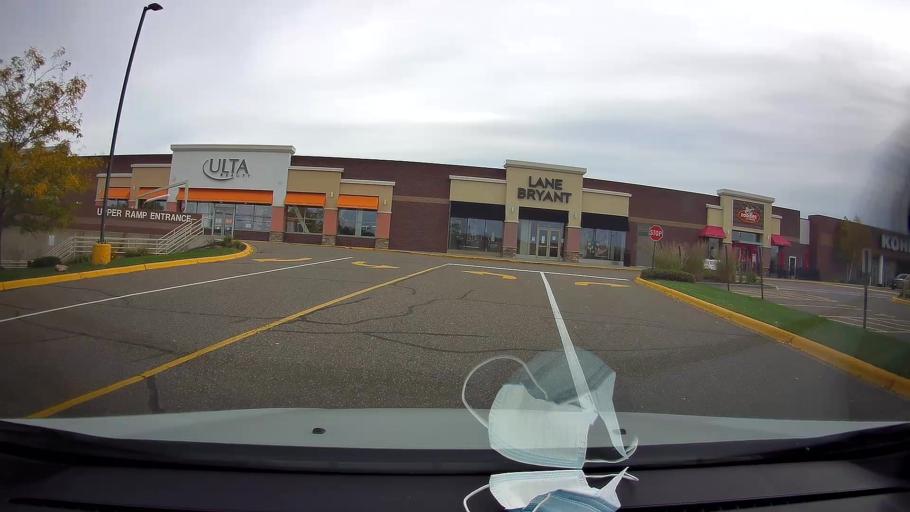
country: US
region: Minnesota
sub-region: Ramsey County
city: Roseville
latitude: 45.0159
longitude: -93.1709
